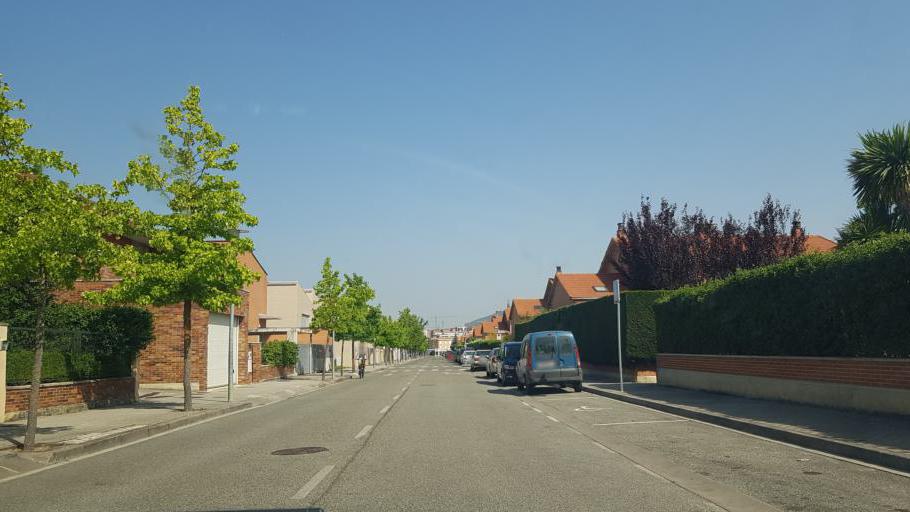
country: ES
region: Navarre
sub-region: Provincia de Navarra
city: Segundo Ensanche
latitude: 42.7918
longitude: -1.6228
